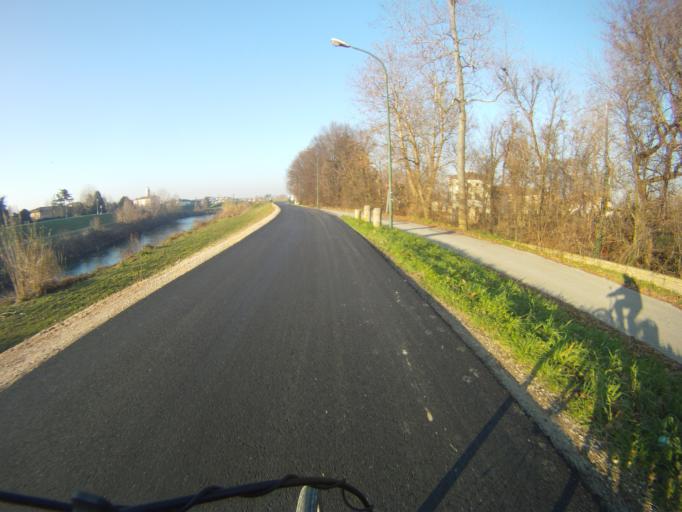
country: IT
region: Veneto
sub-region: Provincia di Padova
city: Legnaro
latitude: 45.3428
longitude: 11.9400
